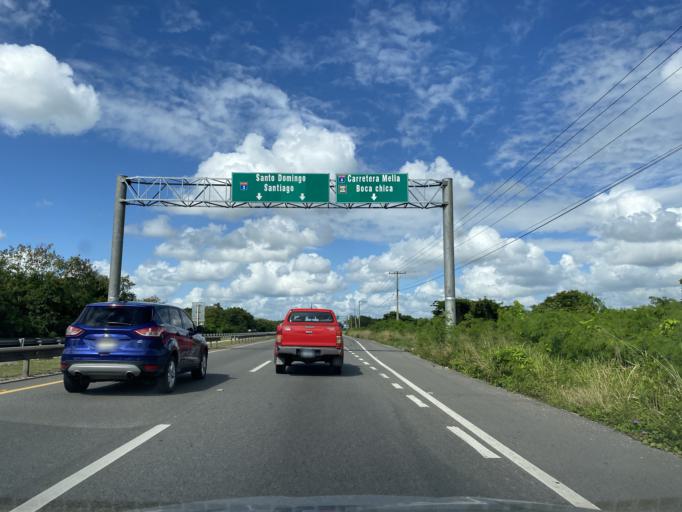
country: DO
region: Santo Domingo
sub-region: Santo Domingo
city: Boca Chica
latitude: 18.4466
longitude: -69.5900
